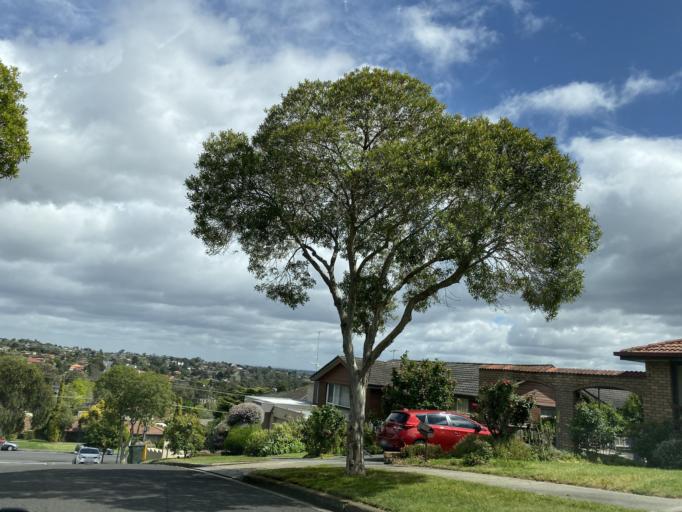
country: AU
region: Victoria
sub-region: Manningham
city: Doncaster East
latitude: -37.7720
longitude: 145.1415
